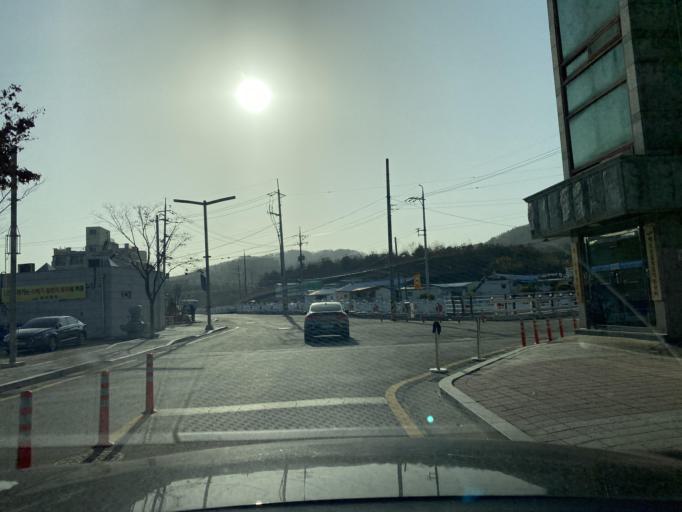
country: KR
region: Chungcheongnam-do
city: Yesan
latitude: 36.6761
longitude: 126.8488
